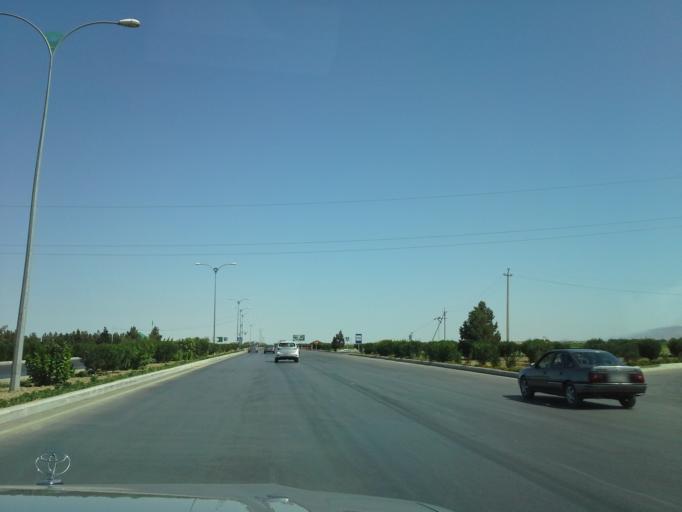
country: TM
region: Ahal
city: Annau
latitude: 37.9071
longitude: 58.5172
